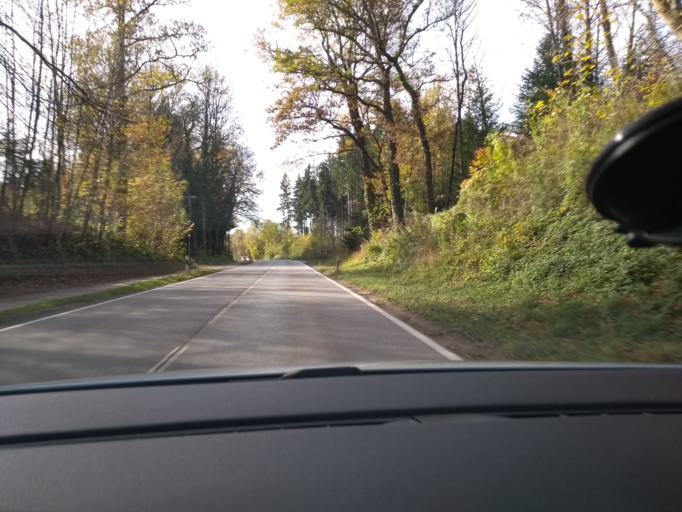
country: DE
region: Bavaria
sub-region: Upper Bavaria
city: Stephanskirchen
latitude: 47.8667
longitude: 12.1687
